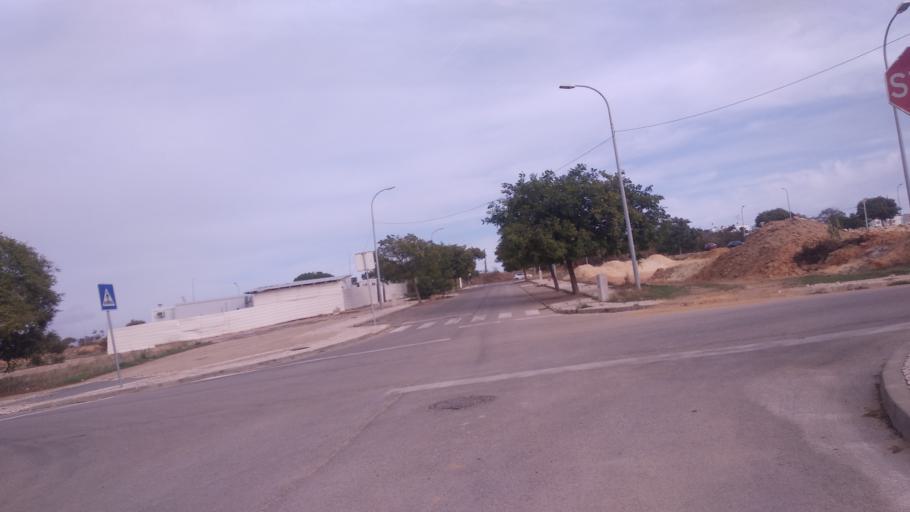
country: PT
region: Faro
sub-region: Faro
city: Faro
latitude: 37.0316
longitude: -7.9380
